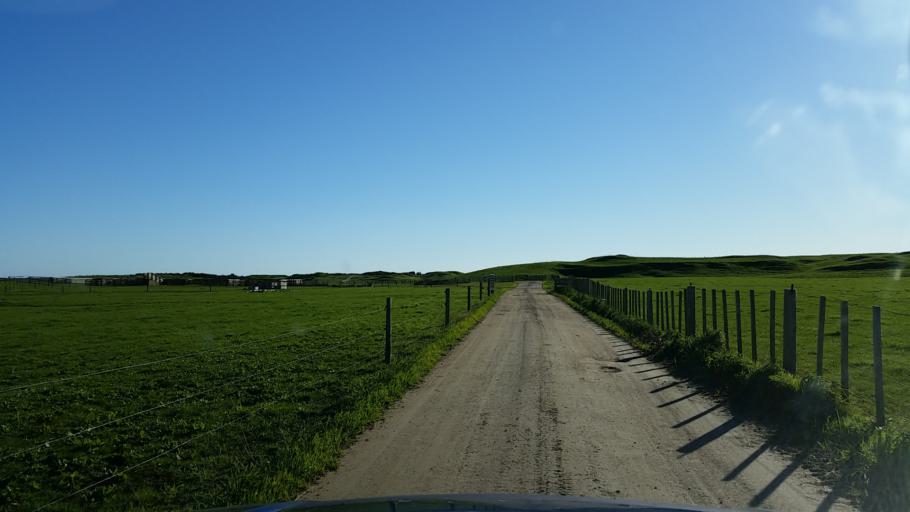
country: NZ
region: Taranaki
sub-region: South Taranaki District
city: Patea
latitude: -39.8371
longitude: 174.7018
